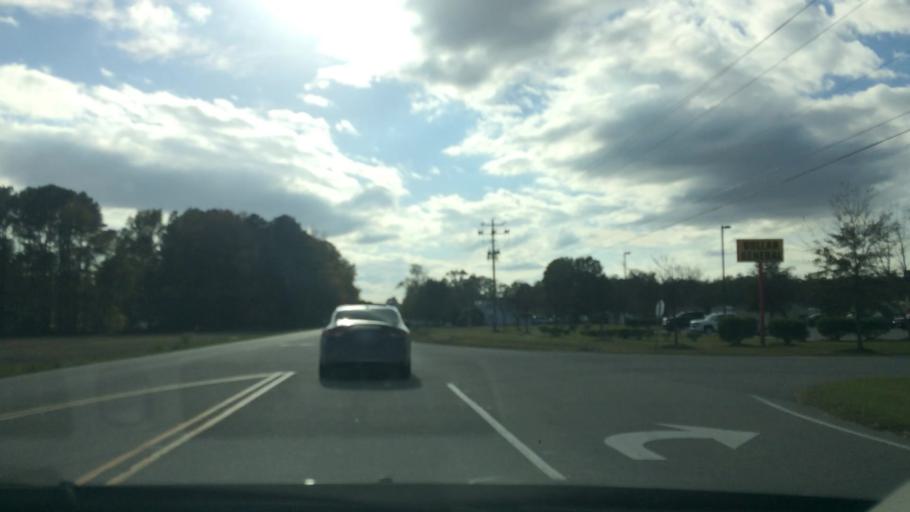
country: US
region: North Carolina
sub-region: Wayne County
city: Elroy
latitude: 35.3982
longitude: -77.9056
